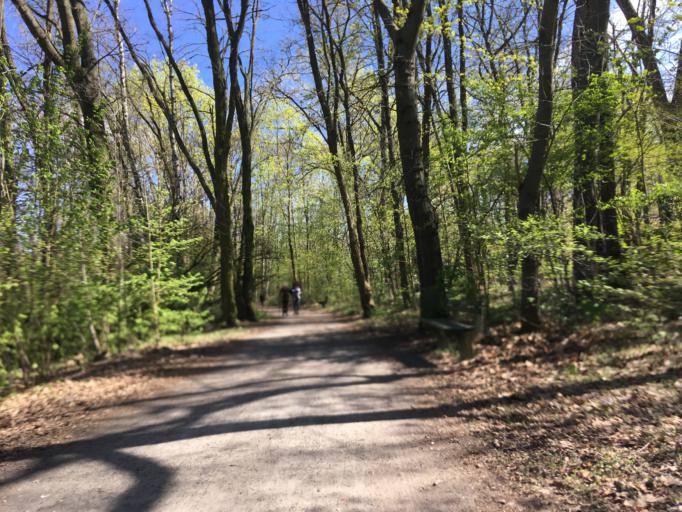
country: DE
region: Berlin
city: Hermsdorf
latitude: 52.6044
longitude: 13.3029
